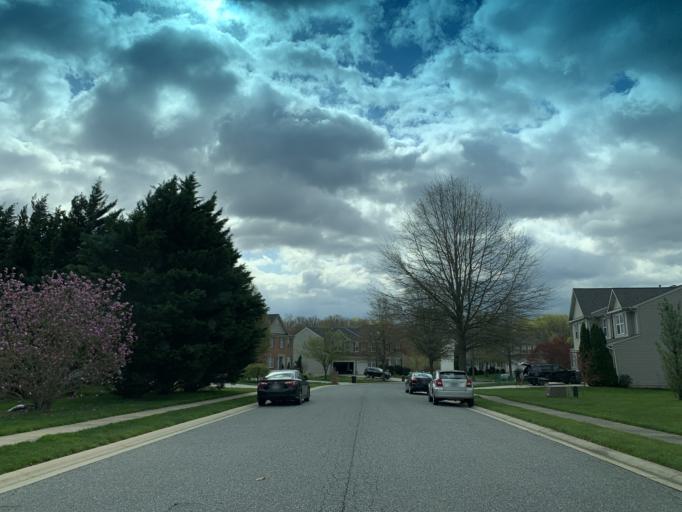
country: US
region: Maryland
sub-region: Harford County
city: South Bel Air
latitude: 39.5532
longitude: -76.3060
